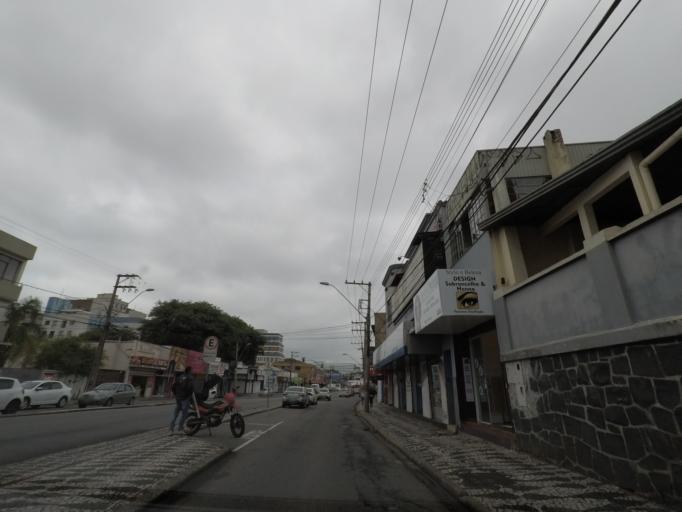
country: BR
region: Parana
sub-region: Curitiba
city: Curitiba
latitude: -25.4740
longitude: -49.2939
